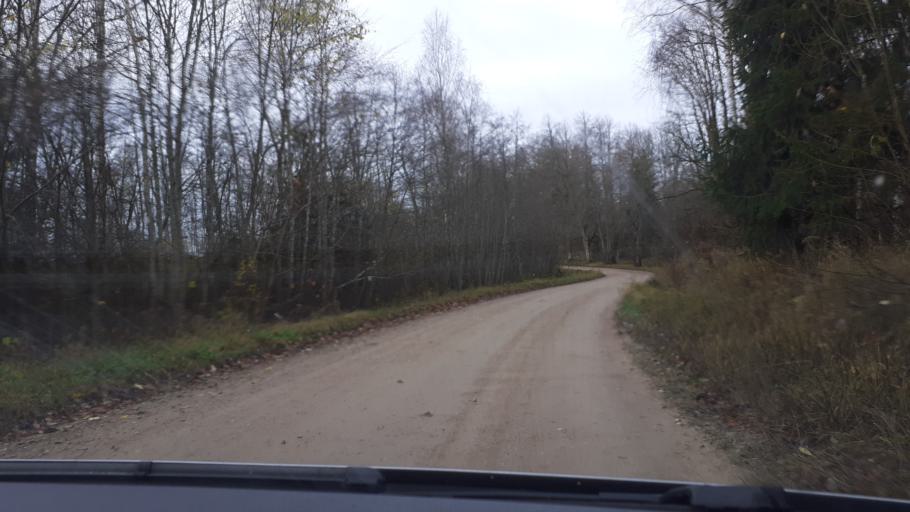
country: LV
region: Aizpute
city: Aizpute
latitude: 56.7730
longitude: 21.8140
